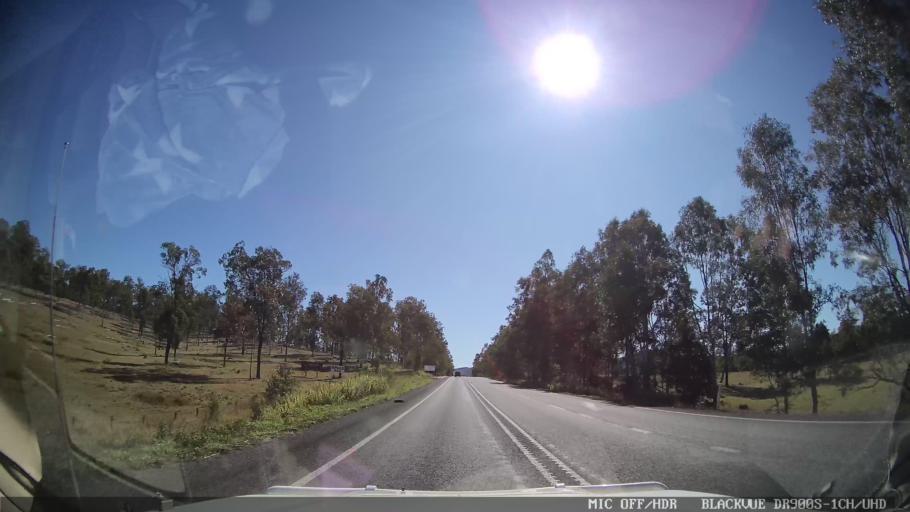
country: AU
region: Queensland
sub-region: Gympie Regional Council
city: Gympie
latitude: -26.0023
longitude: 152.5666
